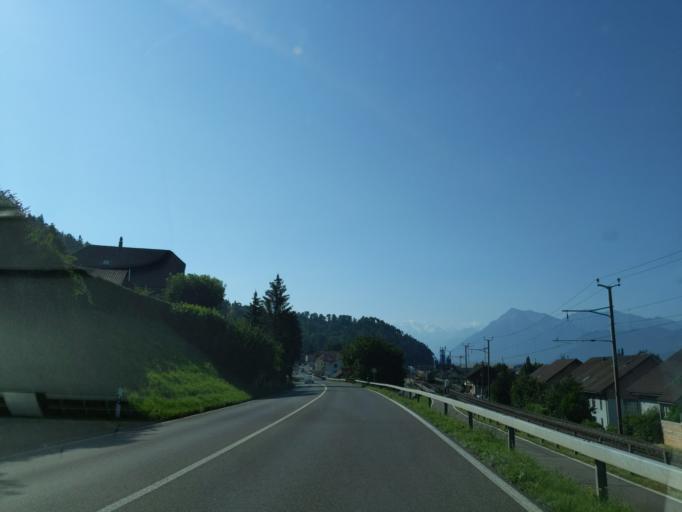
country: CH
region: Bern
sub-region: Thun District
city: Heimberg
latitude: 46.7941
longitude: 7.6041
